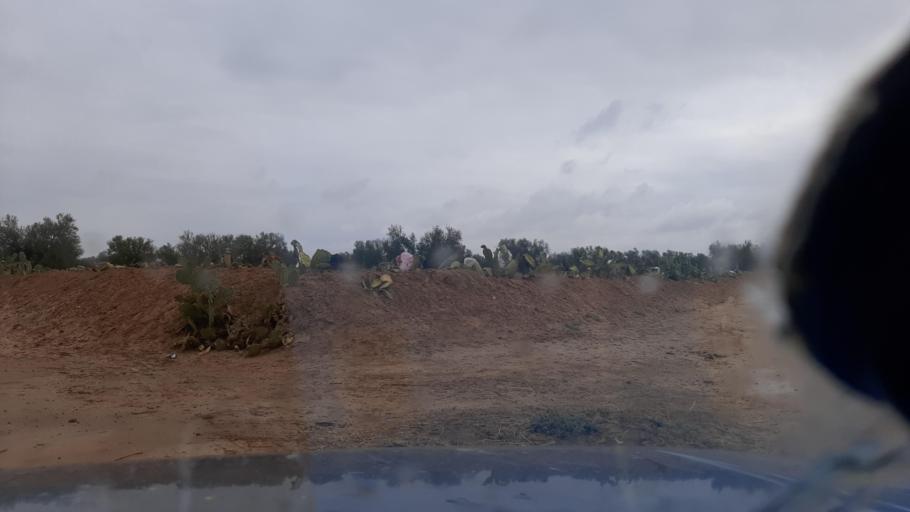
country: TN
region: Al Mahdiyah
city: Shurban
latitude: 35.4350
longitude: 10.4056
